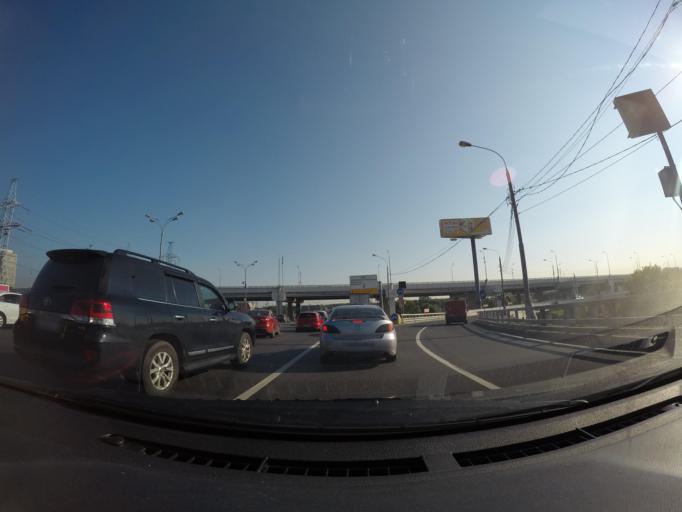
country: RU
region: Moscow
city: Zhulebino
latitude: 55.7110
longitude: 37.8370
